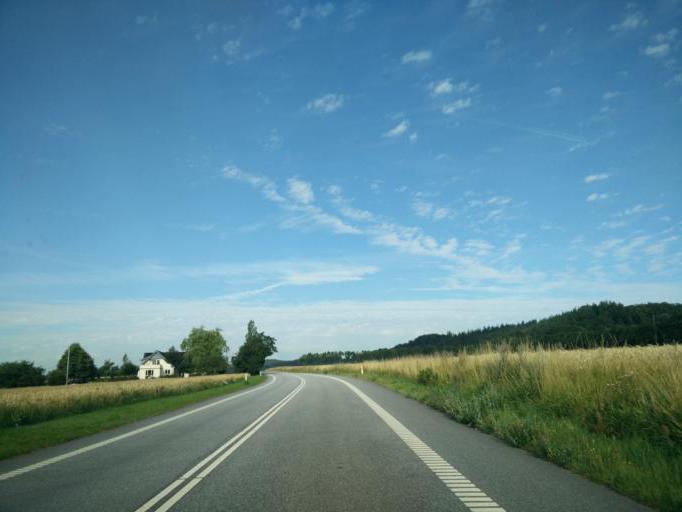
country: DK
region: Central Jutland
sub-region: Favrskov Kommune
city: Ulstrup
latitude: 56.3957
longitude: 9.7832
